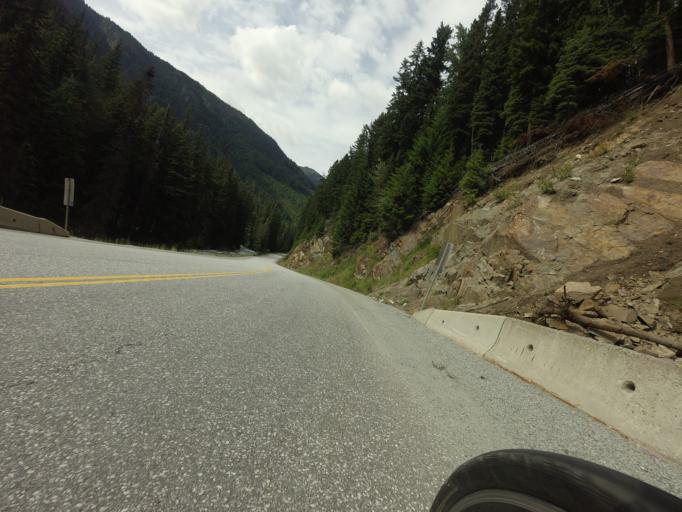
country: CA
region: British Columbia
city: Lillooet
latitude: 50.4378
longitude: -122.2525
